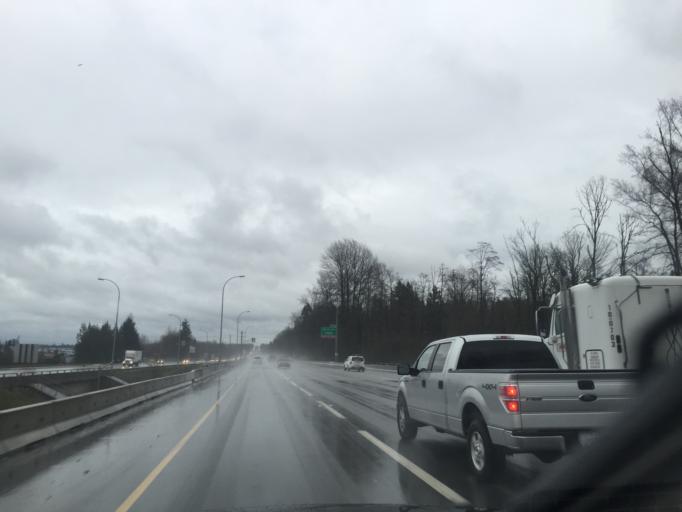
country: CA
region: British Columbia
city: Pitt Meadows
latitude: 49.1767
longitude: -122.7168
